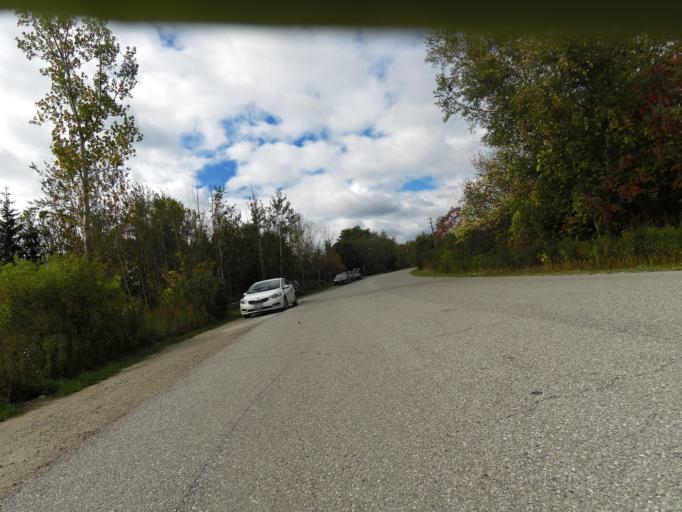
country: CA
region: Ontario
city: Scarborough
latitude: 43.7615
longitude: -79.1609
